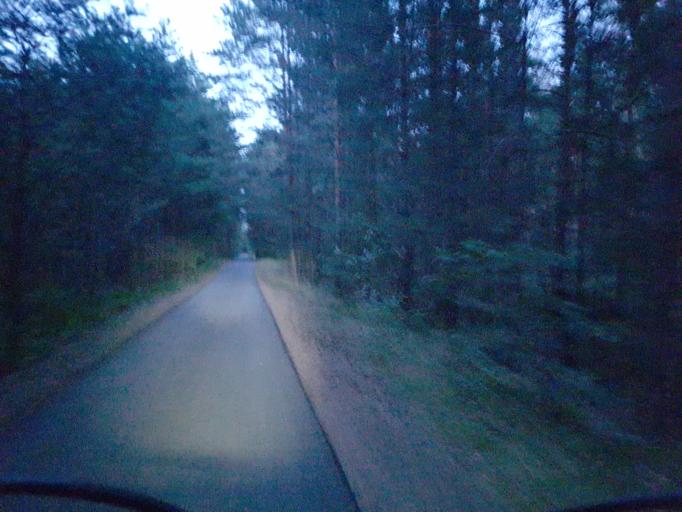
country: DE
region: Brandenburg
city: Trobitz
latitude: 51.5637
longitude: 13.4616
